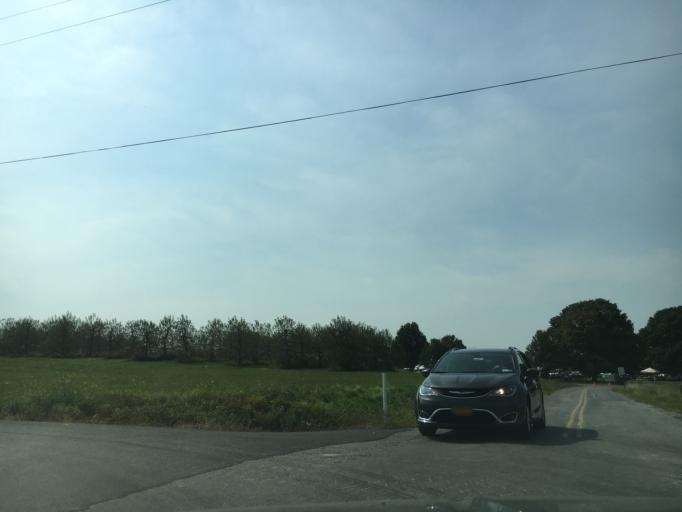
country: US
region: Pennsylvania
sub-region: Berks County
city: Topton
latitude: 40.5509
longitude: -75.7155
